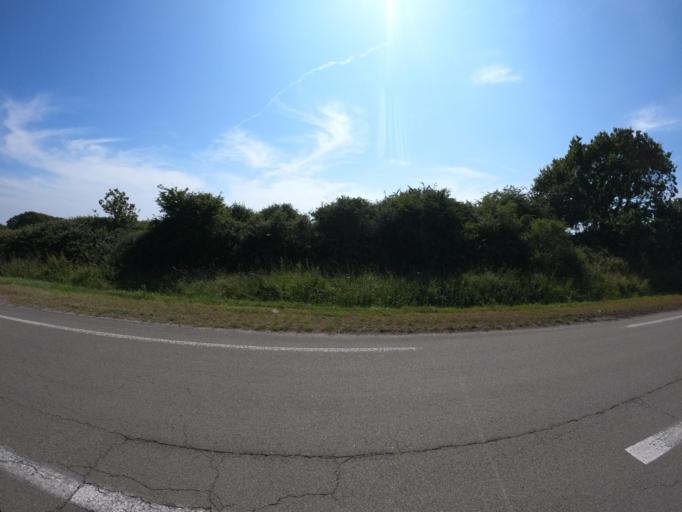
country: FR
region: Pays de la Loire
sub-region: Departement de la Loire-Atlantique
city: La Bernerie-en-Retz
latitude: 47.0901
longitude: -2.0324
